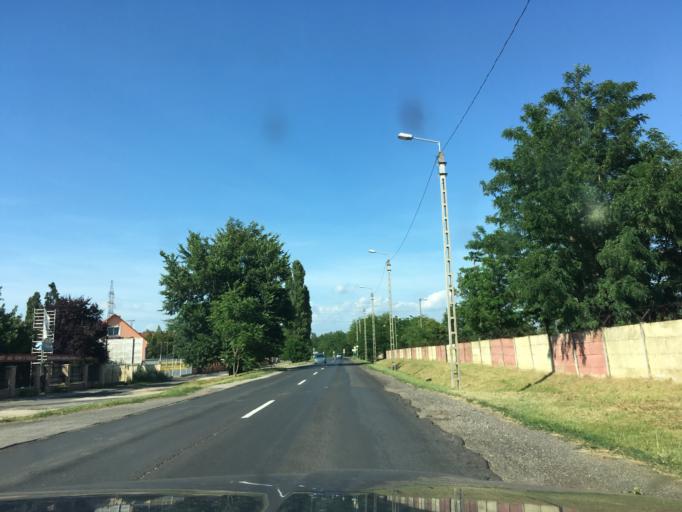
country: HU
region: Hajdu-Bihar
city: Debrecen
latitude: 47.5569
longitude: 21.6699
